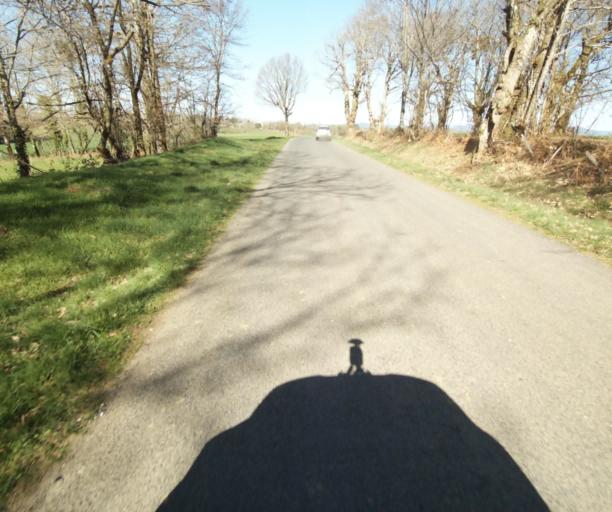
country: FR
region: Limousin
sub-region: Departement de la Correze
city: Chamboulive
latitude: 45.4336
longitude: 1.6683
